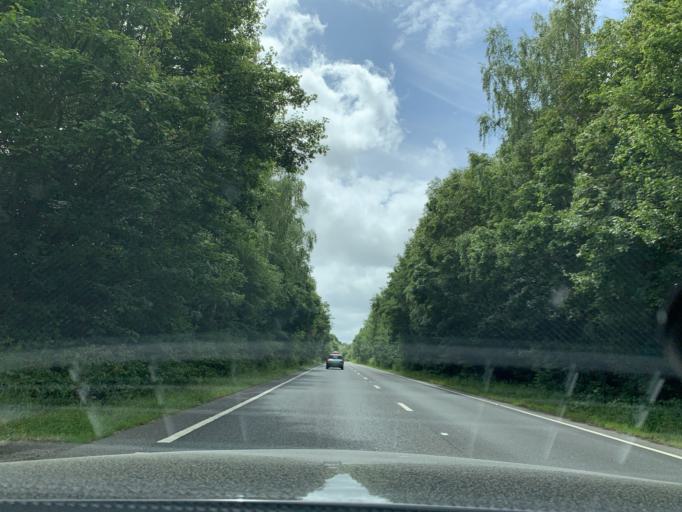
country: GB
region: England
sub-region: East Sussex
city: Robertsbridge
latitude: 50.9840
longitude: 0.4778
